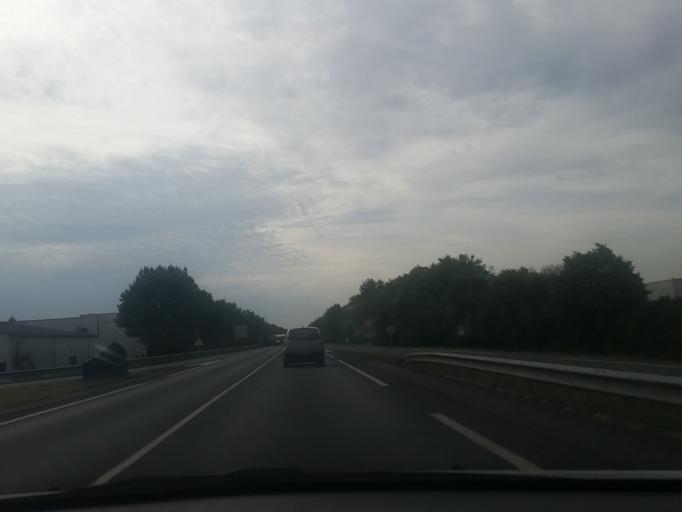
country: FR
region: Pays de la Loire
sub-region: Departement de la Vendee
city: Saint-Fulgent
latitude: 46.8589
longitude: -1.1714
